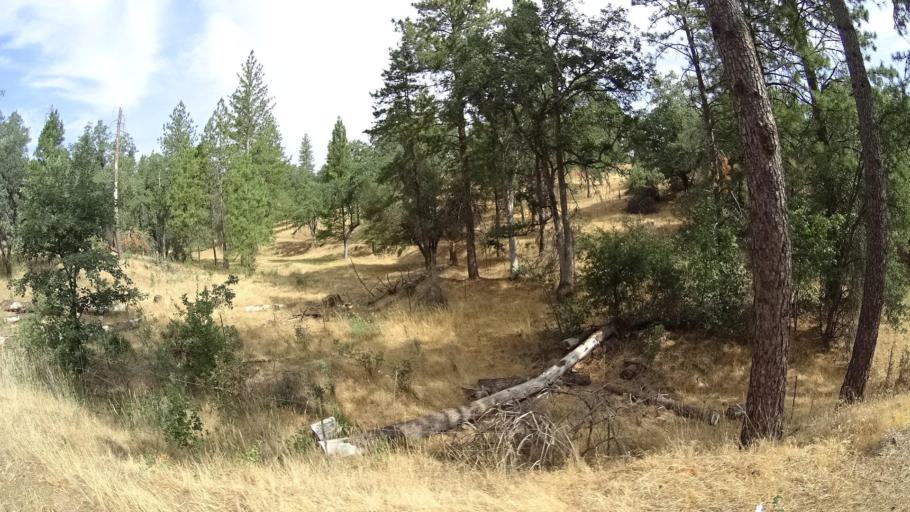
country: US
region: California
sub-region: Mariposa County
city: Mariposa
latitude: 37.5328
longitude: -119.9763
